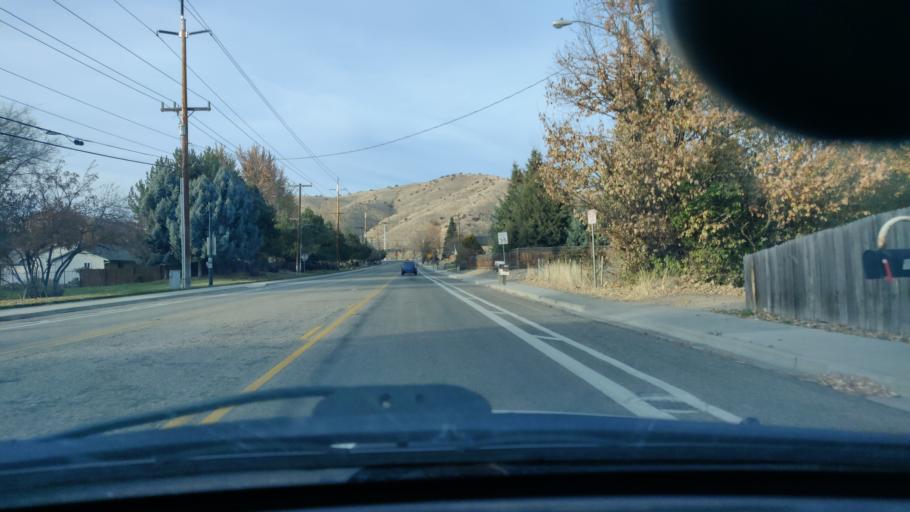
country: US
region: Idaho
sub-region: Ada County
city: Garden City
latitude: 43.6806
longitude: -116.2792
